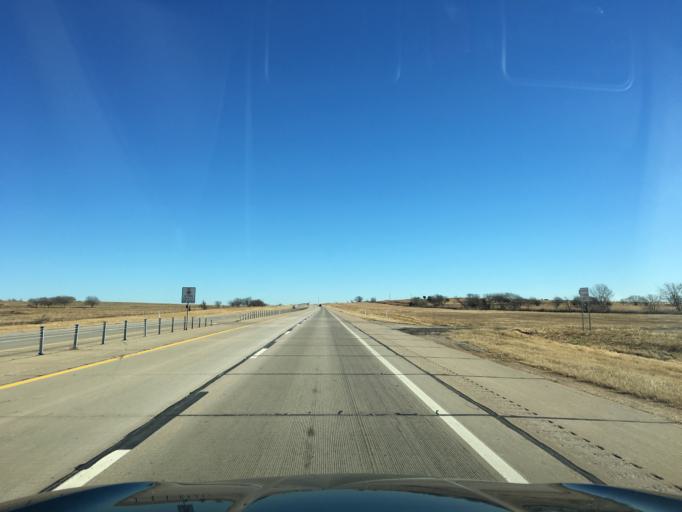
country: US
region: Oklahoma
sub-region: Noble County
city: Perry
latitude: 36.3924
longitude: -97.1895
